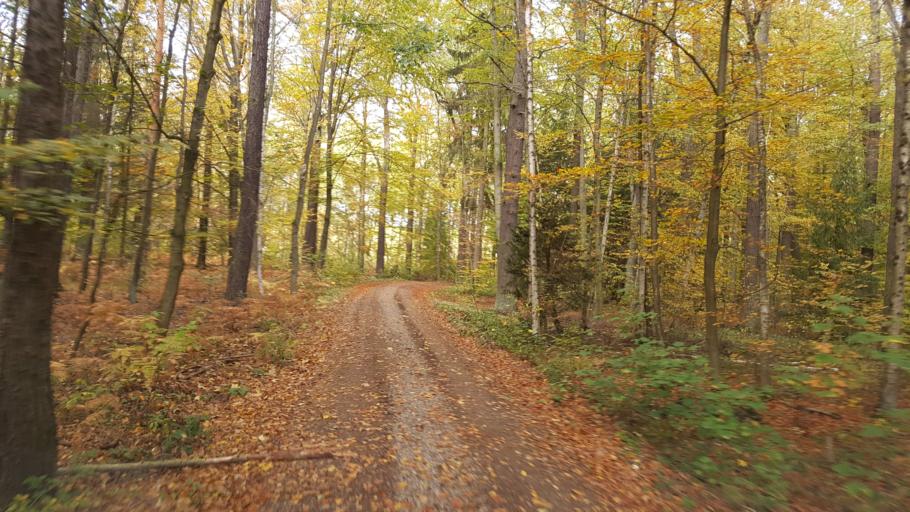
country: DE
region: Brandenburg
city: Doberlug-Kirchhain
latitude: 51.6268
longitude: 13.5249
